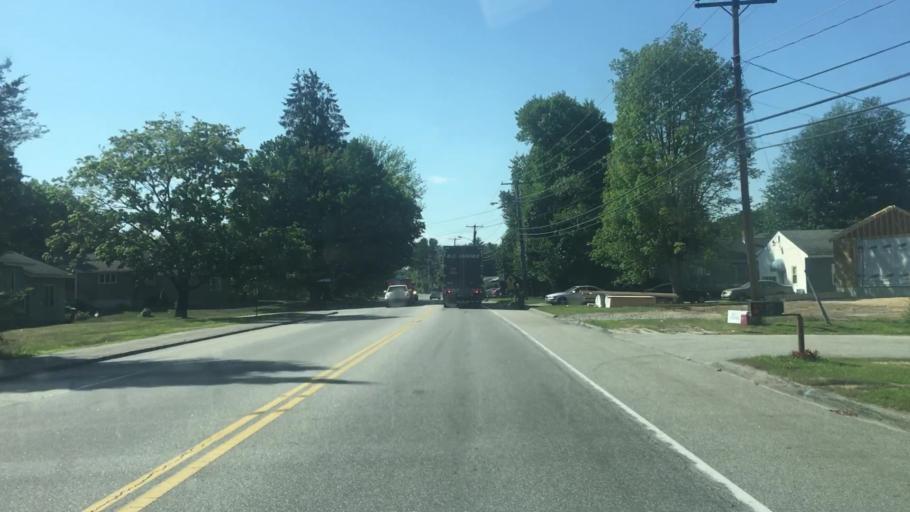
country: US
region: Maine
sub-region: York County
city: Saco
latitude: 43.5239
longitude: -70.4608
